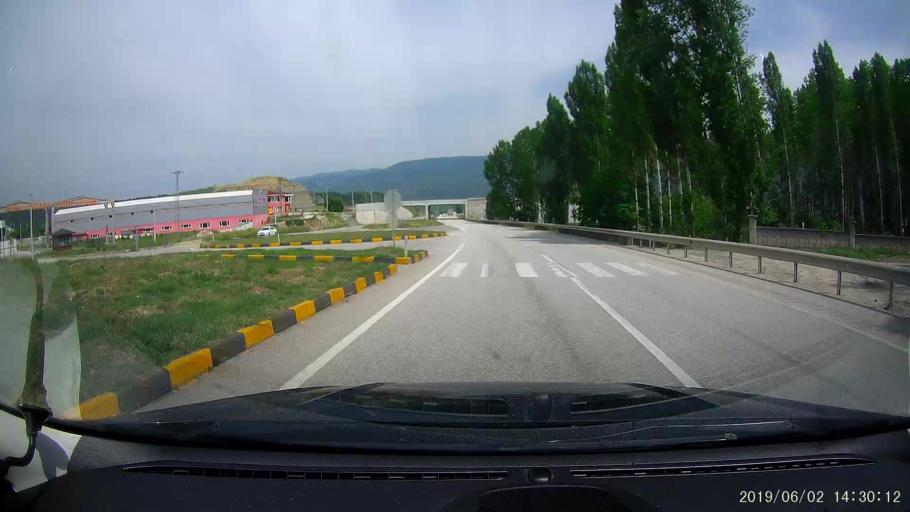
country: TR
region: Kastamonu
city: Tosya
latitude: 41.0191
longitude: 34.1097
